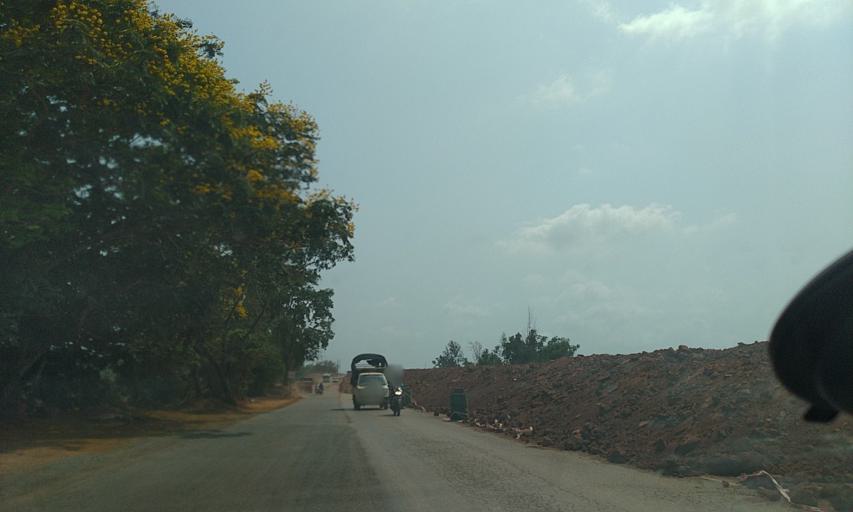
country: IN
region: Goa
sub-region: North Goa
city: Colovale
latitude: 15.6532
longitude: 73.8381
